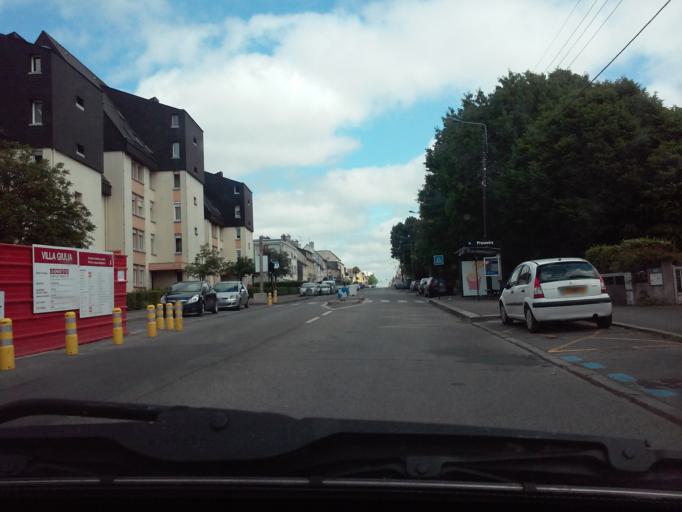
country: FR
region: Brittany
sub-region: Departement d'Ille-et-Vilaine
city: Rennes
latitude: 48.0869
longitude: -1.6948
